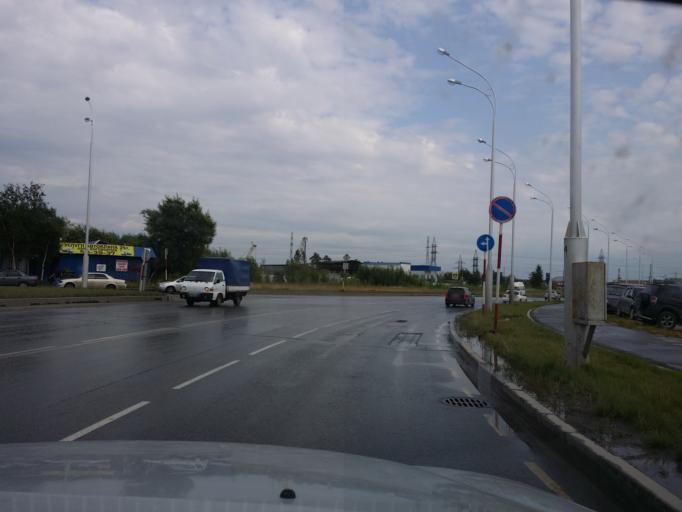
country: RU
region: Khanty-Mansiyskiy Avtonomnyy Okrug
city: Nizhnevartovsk
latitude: 60.9679
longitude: 76.5407
